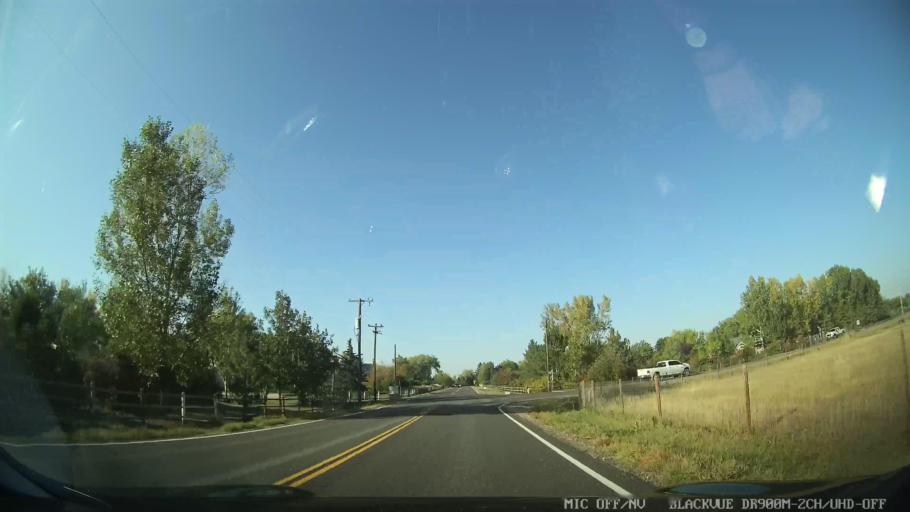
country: US
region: Colorado
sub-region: Larimer County
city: Loveland
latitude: 40.4608
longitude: -105.0567
